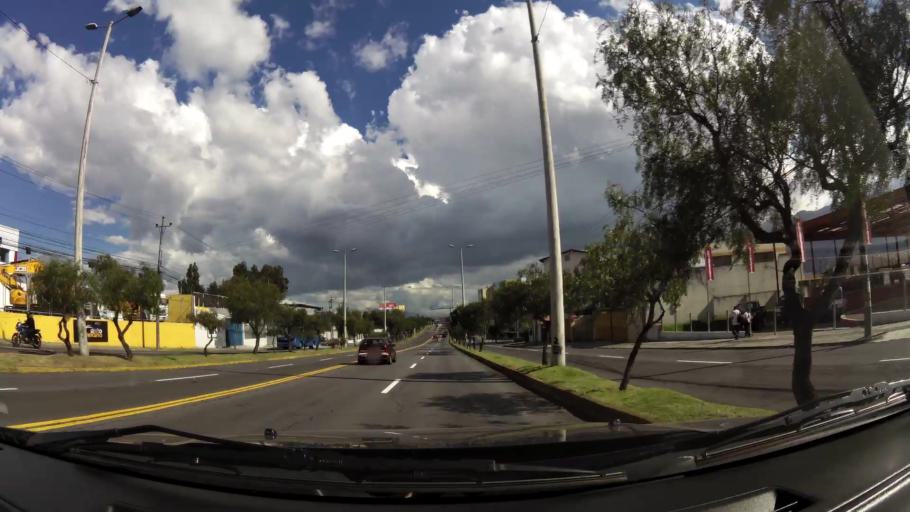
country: EC
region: Pichincha
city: Quito
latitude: -0.1246
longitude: -78.4807
